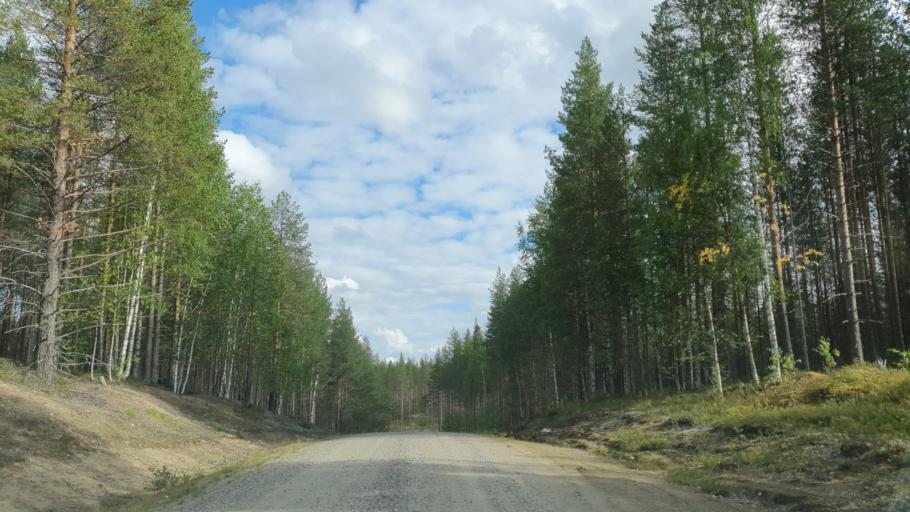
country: FI
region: Kainuu
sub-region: Kehys-Kainuu
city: Kuhmo
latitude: 64.2092
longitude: 29.1694
